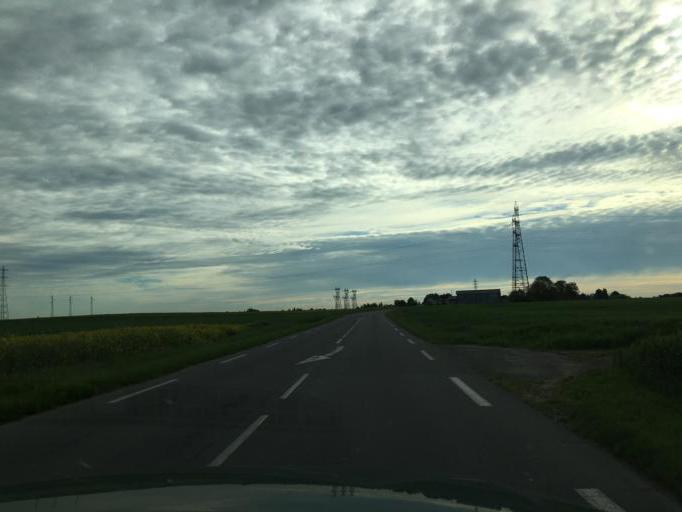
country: FR
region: Centre
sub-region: Departement du Loiret
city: Chaingy
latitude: 47.8911
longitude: 1.7908
